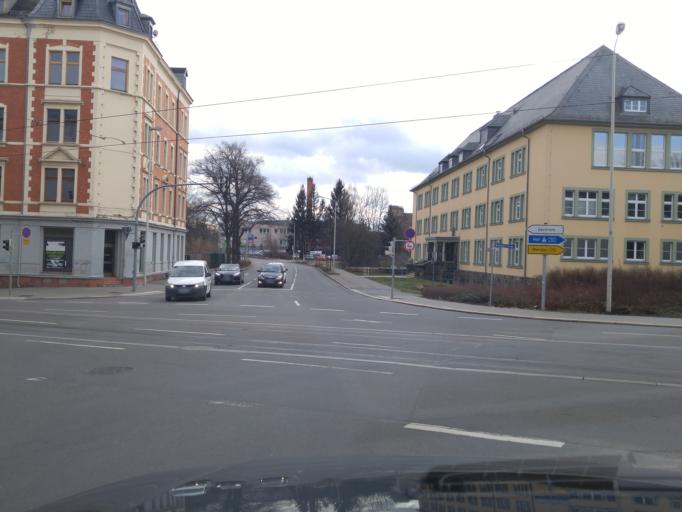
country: DE
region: Saxony
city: Zwickau
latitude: 50.7206
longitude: 12.4764
